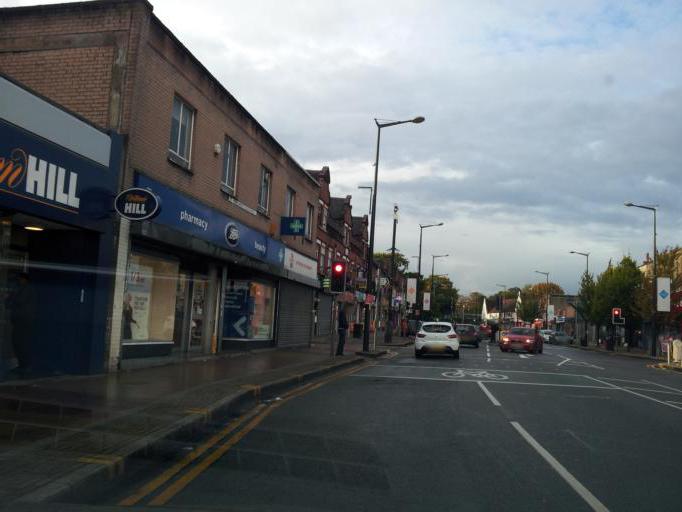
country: GB
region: England
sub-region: Manchester
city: Crumpsall
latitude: 53.5130
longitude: -2.2459
